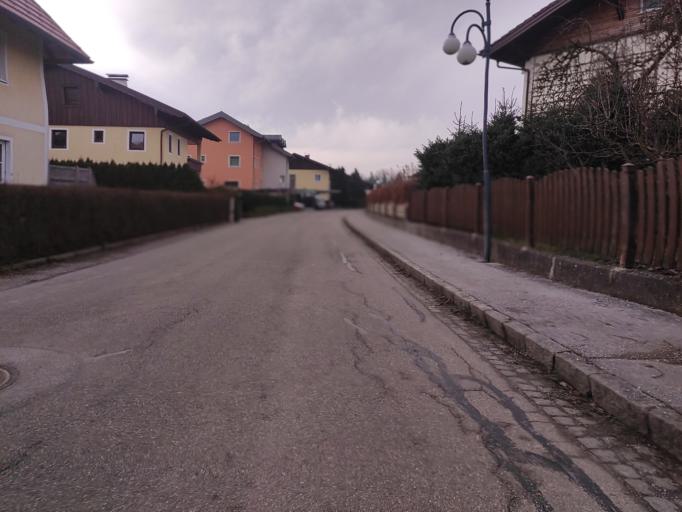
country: AT
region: Salzburg
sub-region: Politischer Bezirk Salzburg-Umgebung
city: Kostendorf
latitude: 47.9597
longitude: 13.2041
